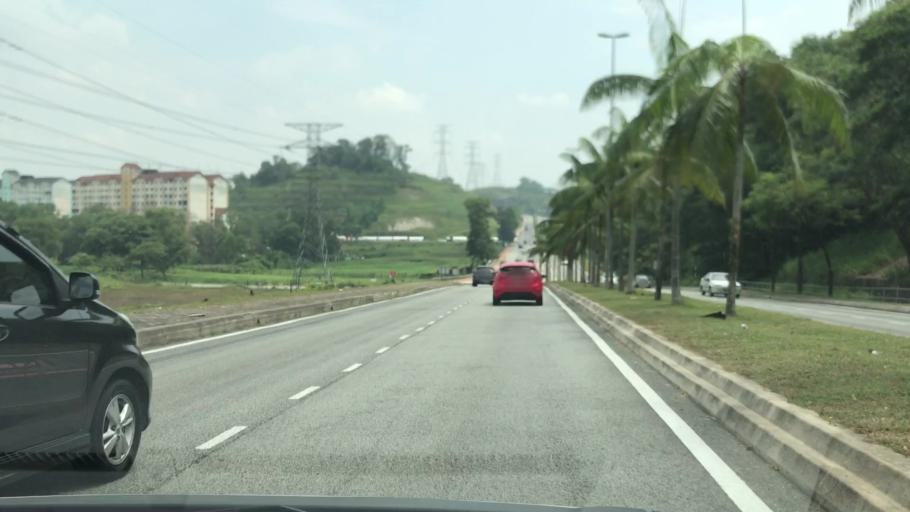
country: MY
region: Selangor
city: Kampong Baharu Balakong
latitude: 3.0330
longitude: 101.6789
